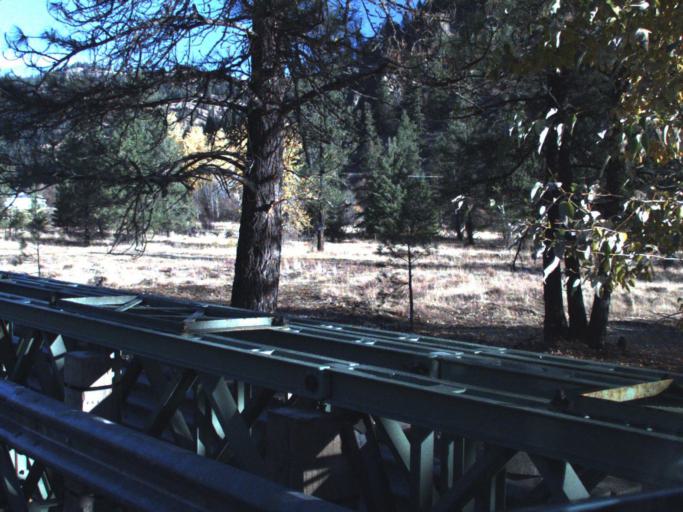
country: US
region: Washington
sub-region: Ferry County
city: Republic
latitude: 48.4589
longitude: -118.7504
